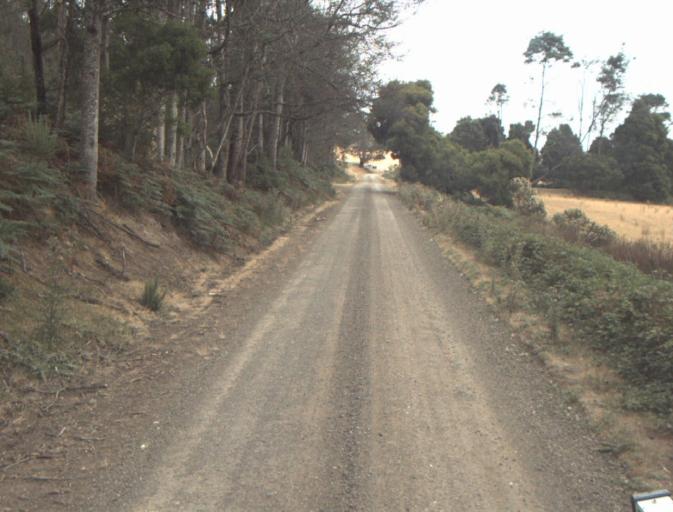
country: AU
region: Tasmania
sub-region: Dorset
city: Bridport
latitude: -41.1927
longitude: 147.2628
